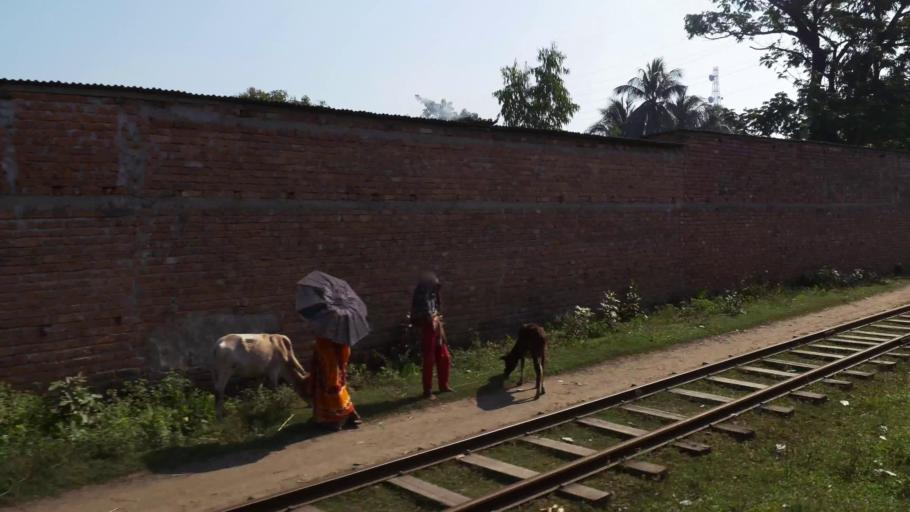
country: BD
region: Dhaka
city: Mymensingh
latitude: 24.6129
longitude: 90.4819
